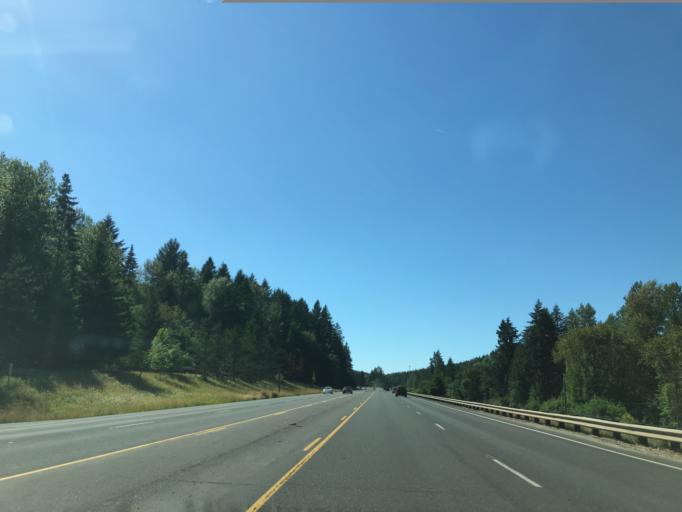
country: US
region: Oregon
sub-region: Linn County
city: Sweet Home
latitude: 44.4014
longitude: -122.7446
